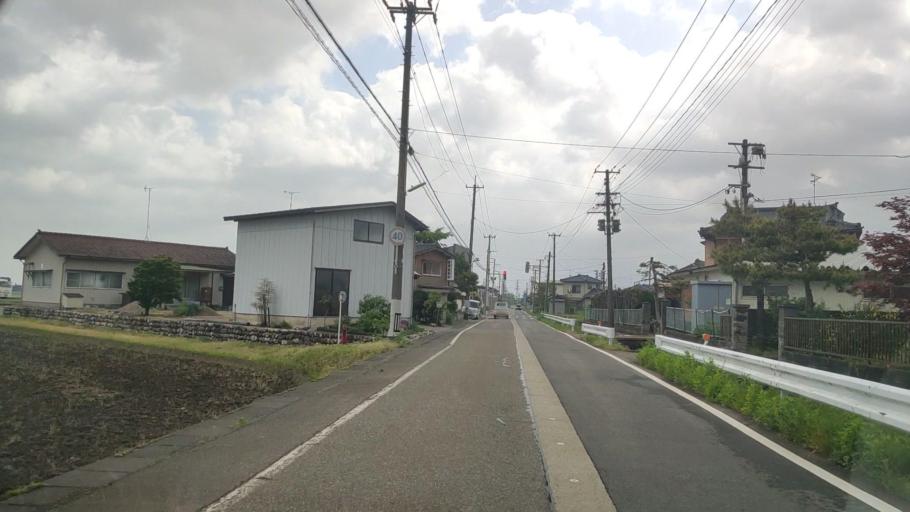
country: JP
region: Niigata
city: Gosen
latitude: 37.7343
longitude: 139.1653
